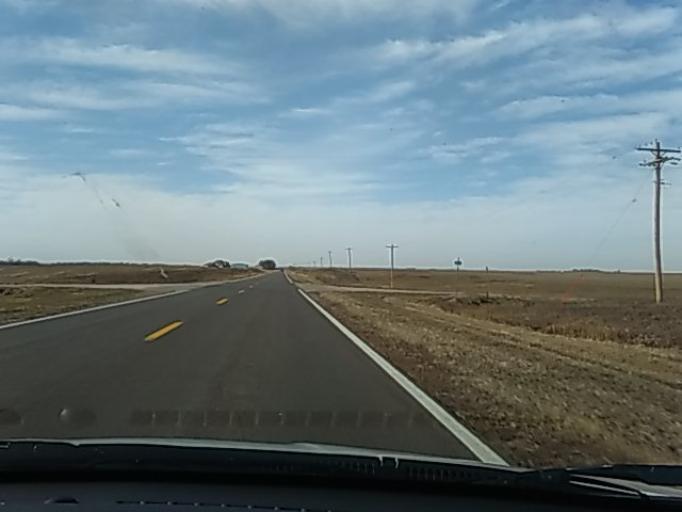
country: US
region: Nebraska
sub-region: Clay County
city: Clay Center
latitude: 40.4232
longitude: -97.9754
